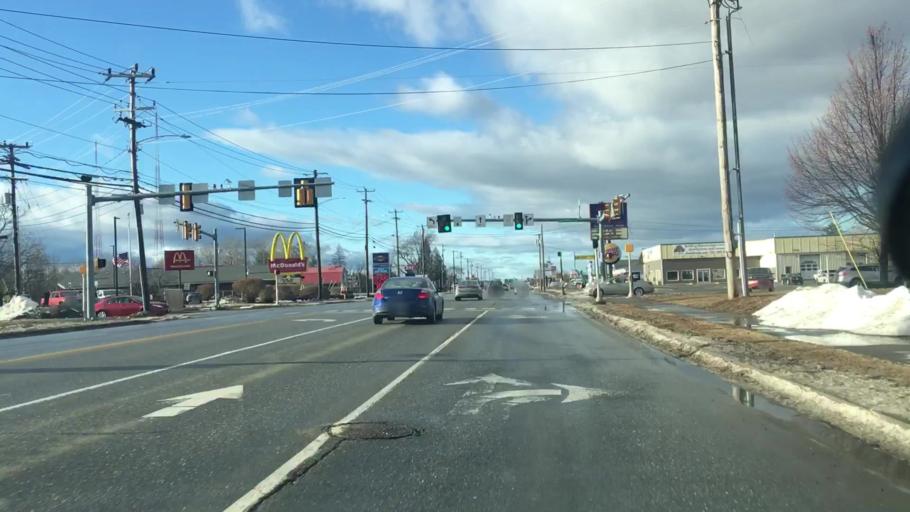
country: US
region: Maine
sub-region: Penobscot County
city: Brewer
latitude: 44.7803
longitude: -68.7423
